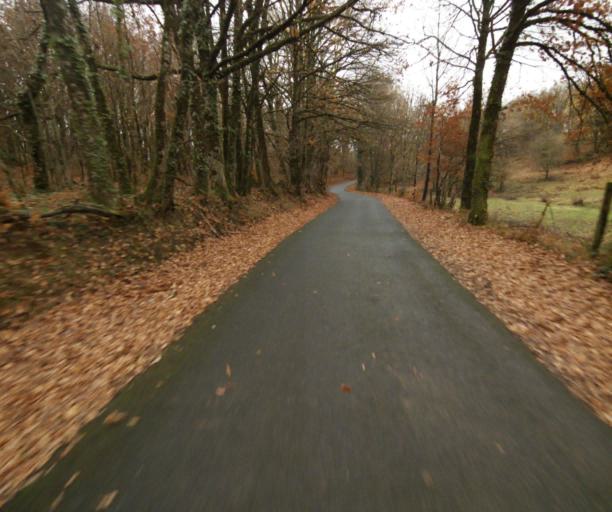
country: FR
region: Limousin
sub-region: Departement de la Correze
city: Saint-Mexant
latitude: 45.2940
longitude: 1.6334
